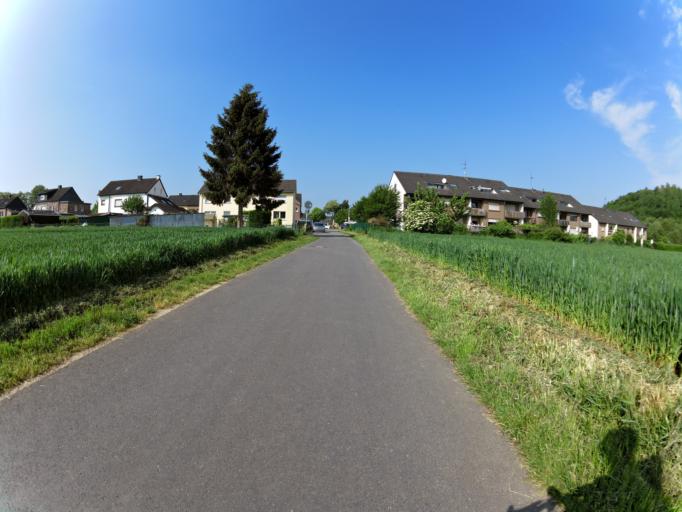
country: DE
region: North Rhine-Westphalia
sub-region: Regierungsbezirk Koln
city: Alsdorf
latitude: 50.8674
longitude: 6.1944
